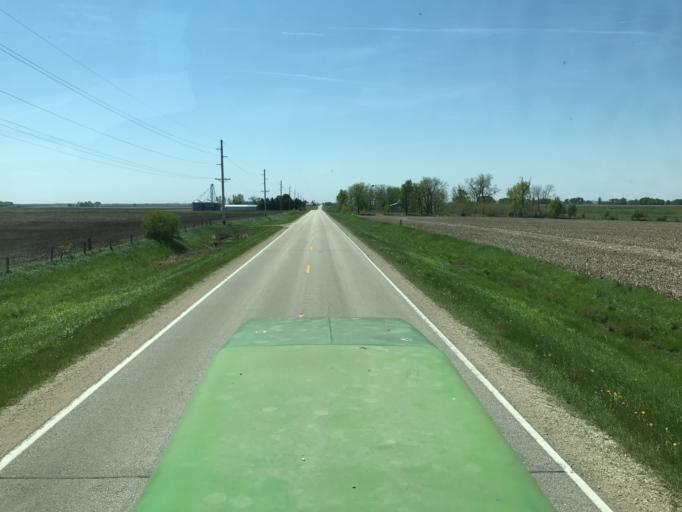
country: US
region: Iowa
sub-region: Butler County
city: Shell Rock
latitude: 42.6773
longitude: -92.5936
